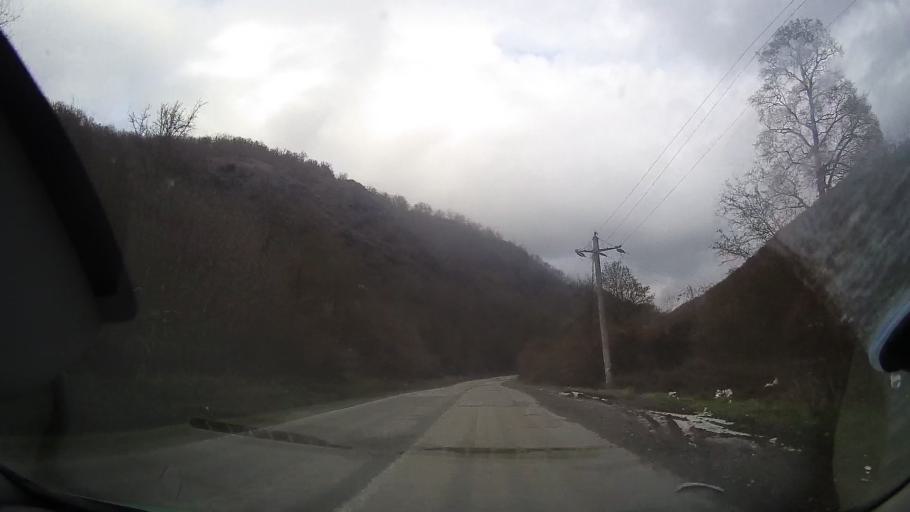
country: RO
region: Cluj
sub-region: Comuna Moldovenesti
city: Moldovenesti
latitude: 46.5036
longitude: 23.6290
